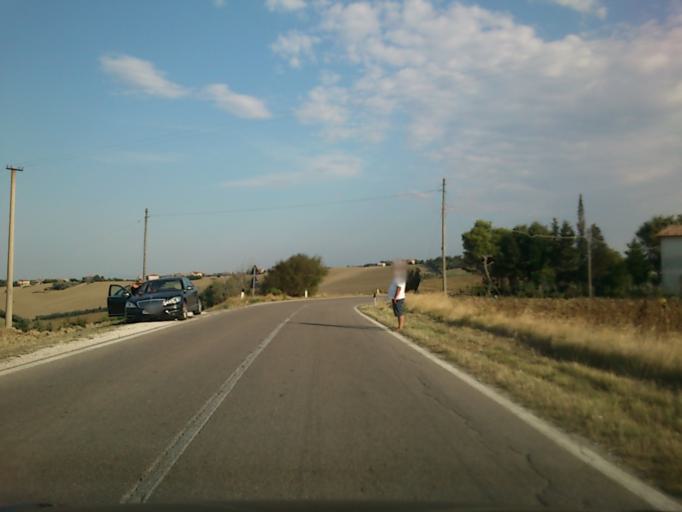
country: IT
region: The Marches
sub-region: Provincia di Pesaro e Urbino
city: San Costanzo
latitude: 43.7887
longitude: 13.0671
